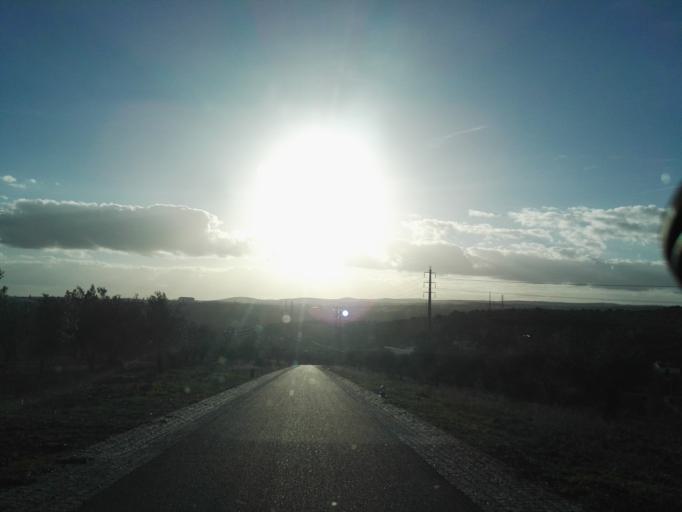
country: PT
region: Portalegre
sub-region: Elvas
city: Elvas
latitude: 38.8931
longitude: -7.1684
